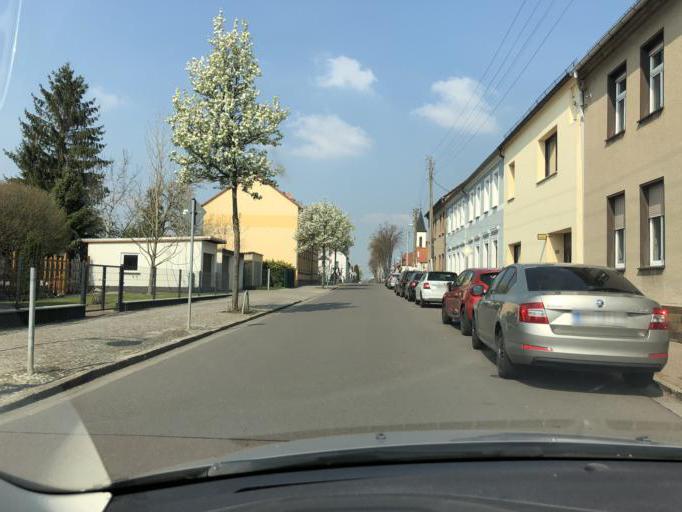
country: DE
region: Saxony-Anhalt
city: Zorbig
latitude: 51.6300
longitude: 12.1224
